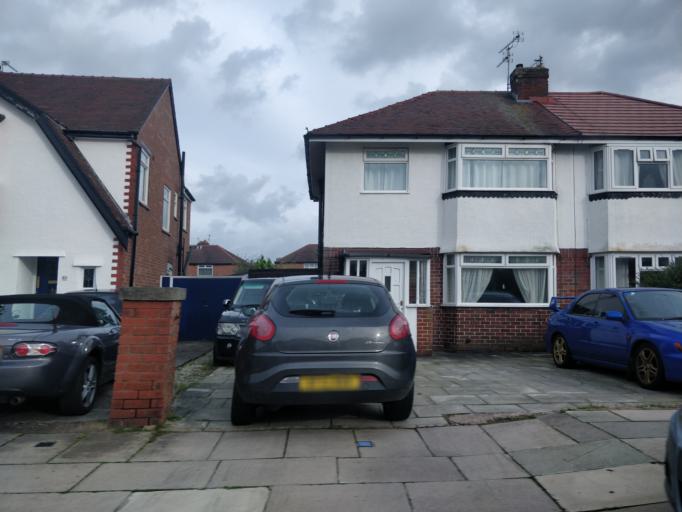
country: GB
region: England
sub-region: Lancashire
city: Banks
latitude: 53.6687
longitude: -2.9558
